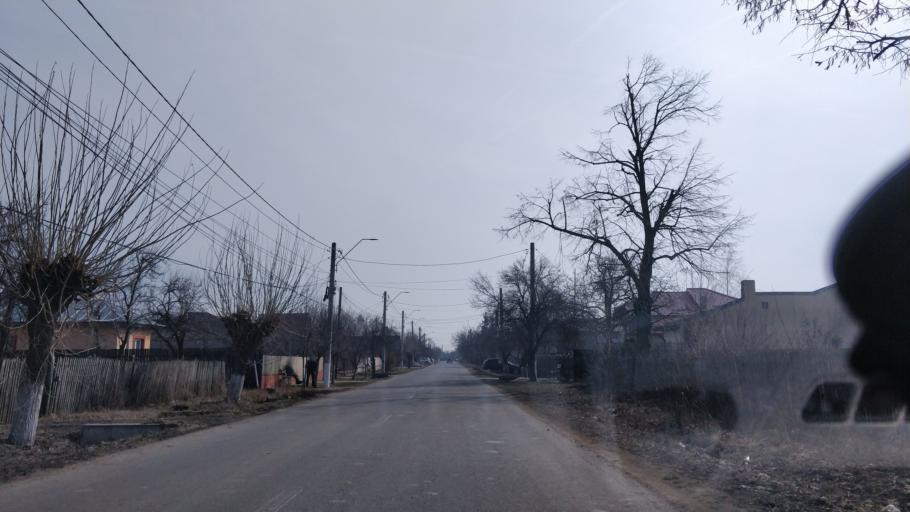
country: RO
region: Giurgiu
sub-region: Comuna Ulmi
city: Ulmi
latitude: 44.4631
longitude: 25.7772
